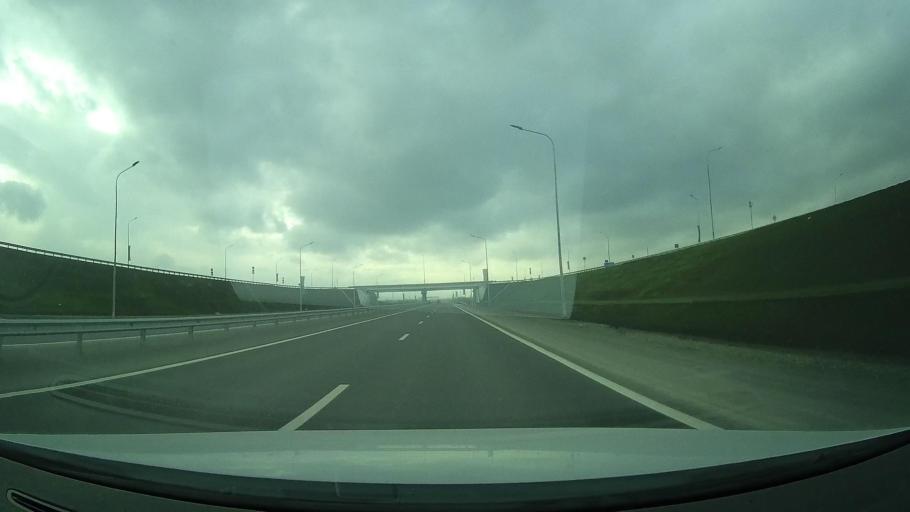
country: RU
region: Rostov
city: Grushevskaya
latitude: 47.4845
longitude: 39.9319
